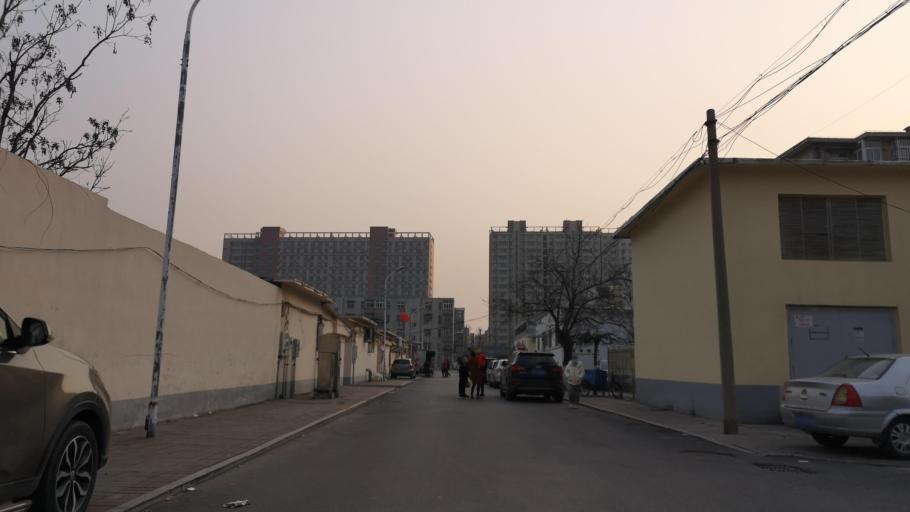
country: CN
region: Henan Sheng
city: Zhongyuanlu
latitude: 35.7662
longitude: 115.1013
